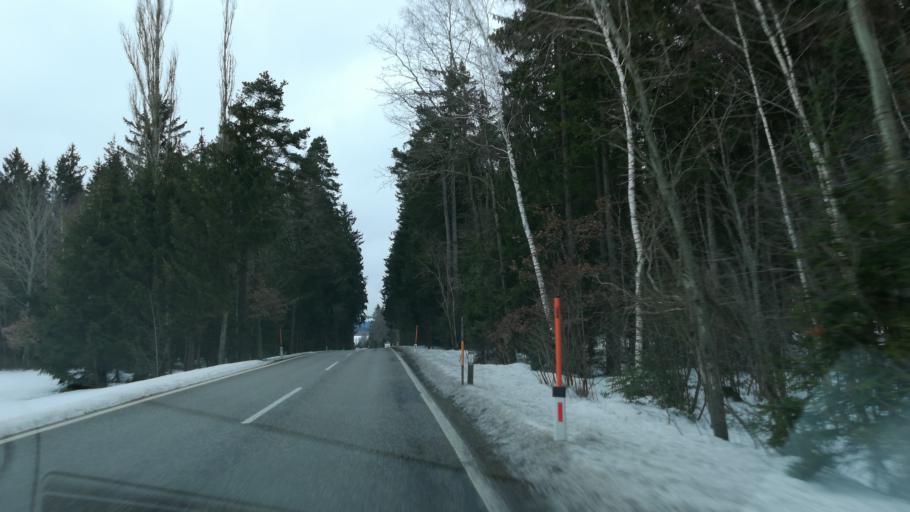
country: AT
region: Upper Austria
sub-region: Politischer Bezirk Urfahr-Umgebung
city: Herzogsdorf
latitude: 48.4443
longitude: 14.1199
